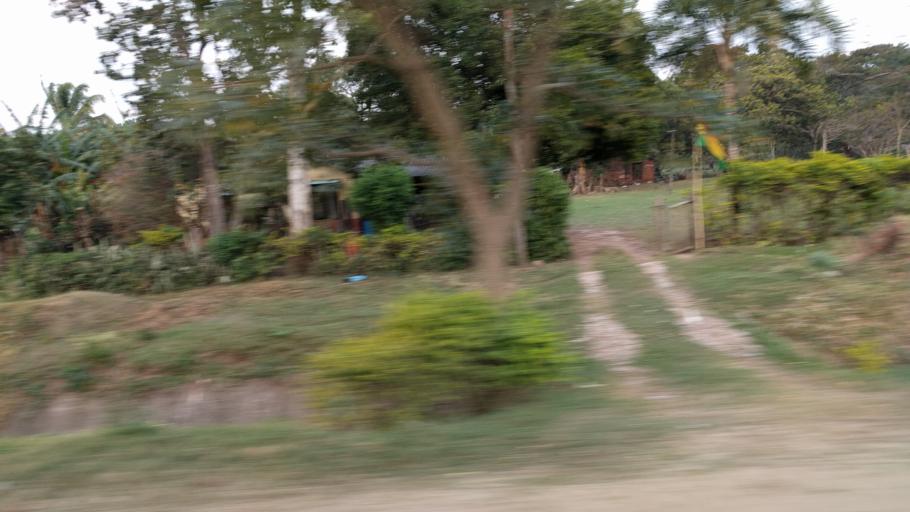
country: BO
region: Santa Cruz
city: Santa Rita
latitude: -17.9725
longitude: -63.3649
